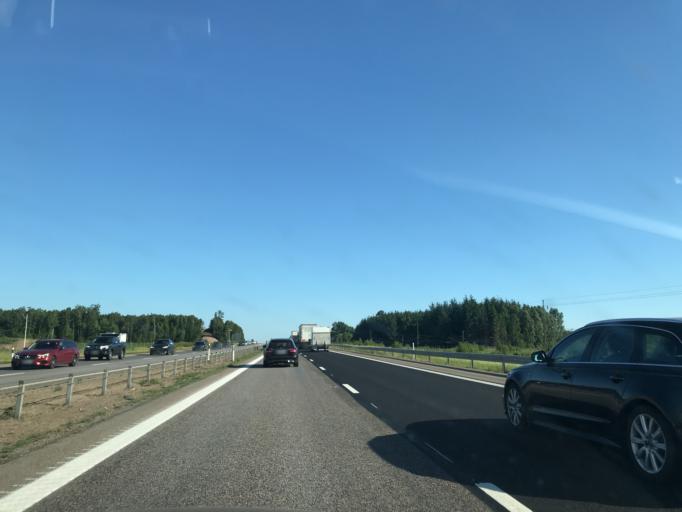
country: SE
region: Halland
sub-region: Halmstads Kommun
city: Halmstad
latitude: 56.7219
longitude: 12.8844
